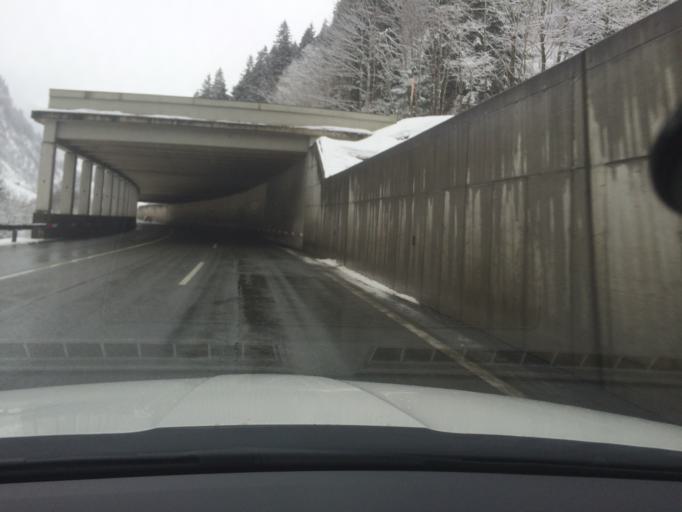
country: AT
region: Salzburg
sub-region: Politischer Bezirk Zell am See
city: Stuhlfelden
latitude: 47.2158
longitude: 12.5032
